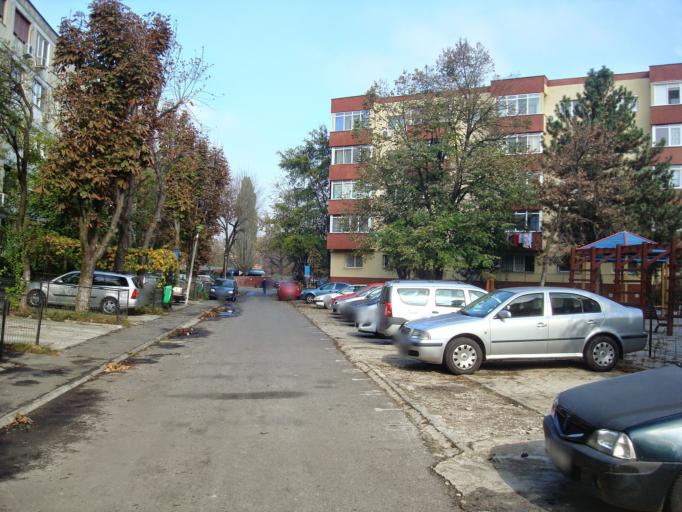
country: RO
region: Bucuresti
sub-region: Municipiul Bucuresti
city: Bucuresti
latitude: 44.3797
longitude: 26.0945
